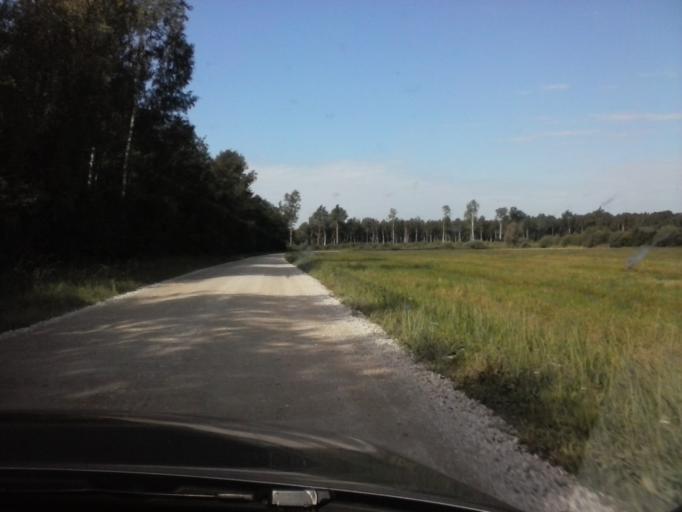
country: EE
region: Laeaene
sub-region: Ridala Parish
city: Uuemoisa
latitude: 58.8813
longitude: 23.5894
